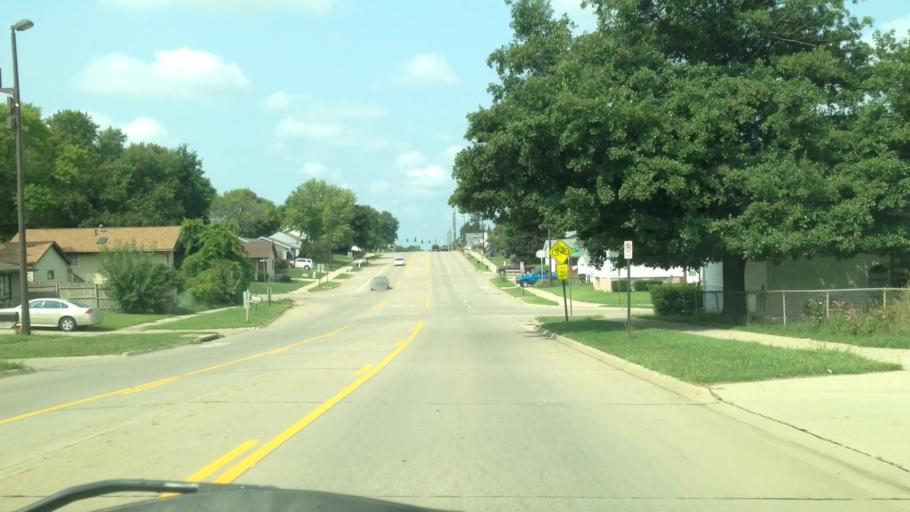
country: US
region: Iowa
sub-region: Linn County
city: Fairfax
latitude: 41.9456
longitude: -91.7103
